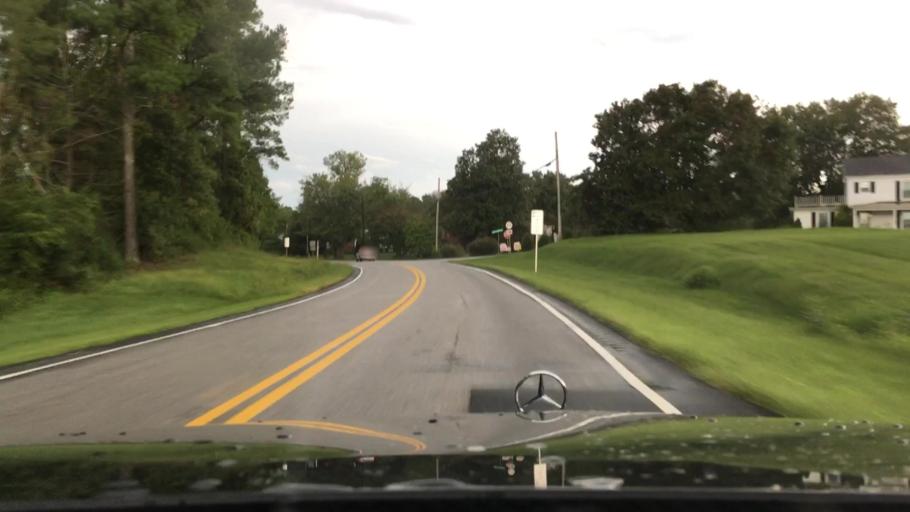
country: US
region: Virginia
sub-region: Amherst County
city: Amherst
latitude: 37.6449
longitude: -79.0217
